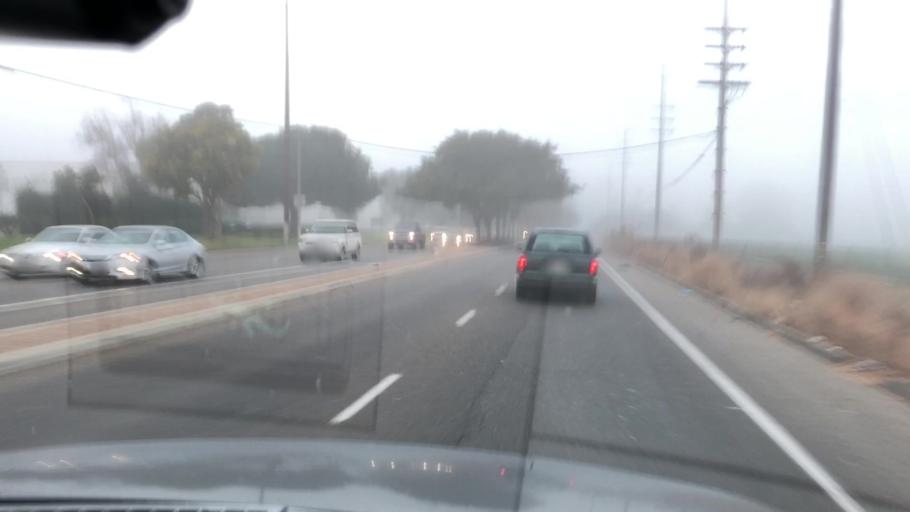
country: US
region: California
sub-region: Ventura County
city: Oxnard
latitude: 34.1829
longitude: -119.1599
